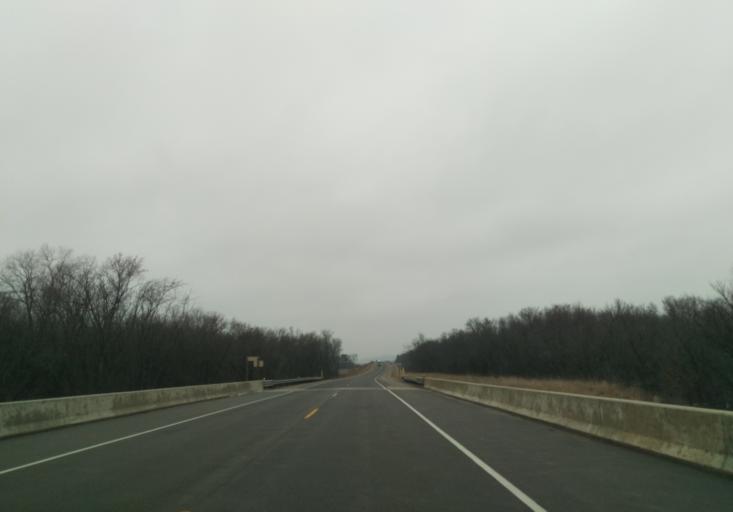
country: US
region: Wisconsin
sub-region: Sauk County
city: Spring Green
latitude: 43.1706
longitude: -90.0440
